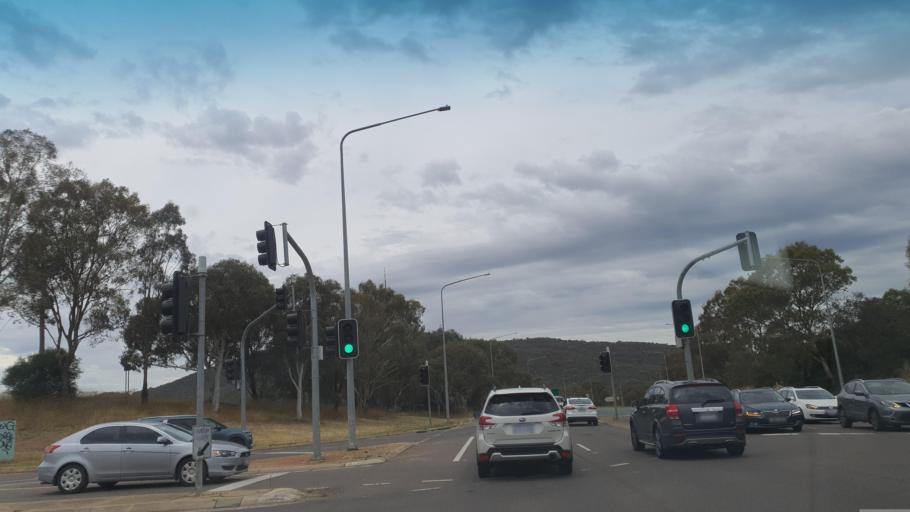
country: AU
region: Australian Capital Territory
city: Macquarie
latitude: -35.2765
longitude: 149.0755
